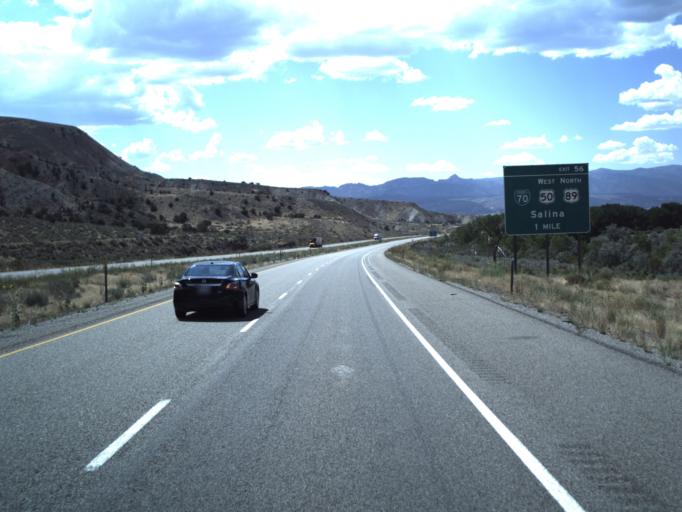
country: US
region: Utah
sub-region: Sevier County
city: Salina
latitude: 38.9306
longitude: -111.8263
